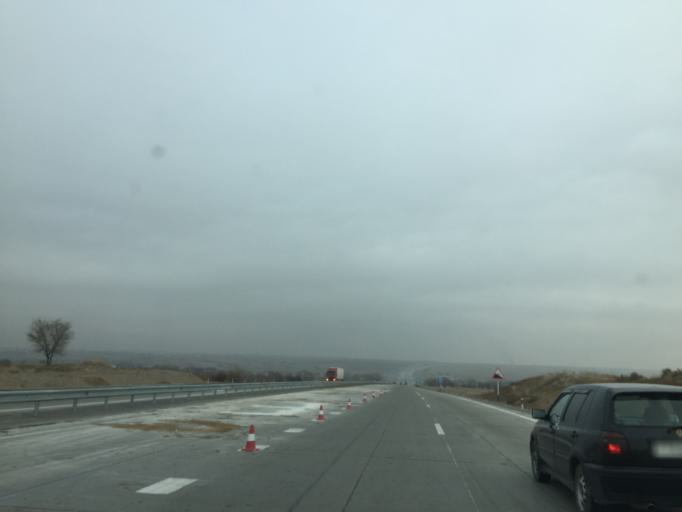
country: KZ
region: Ongtustik Qazaqstan
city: Aksu
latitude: 42.4528
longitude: 69.7501
